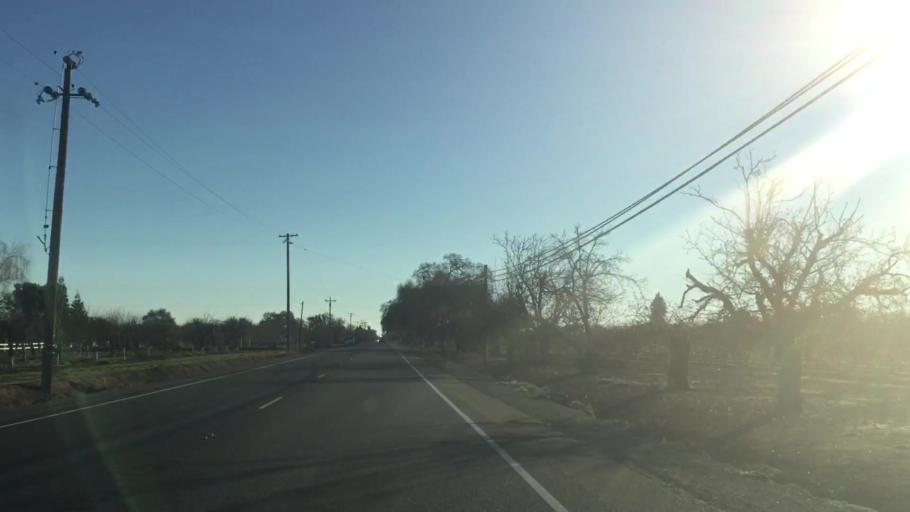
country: US
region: California
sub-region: Sutter County
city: Live Oak
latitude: 39.2473
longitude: -121.5994
